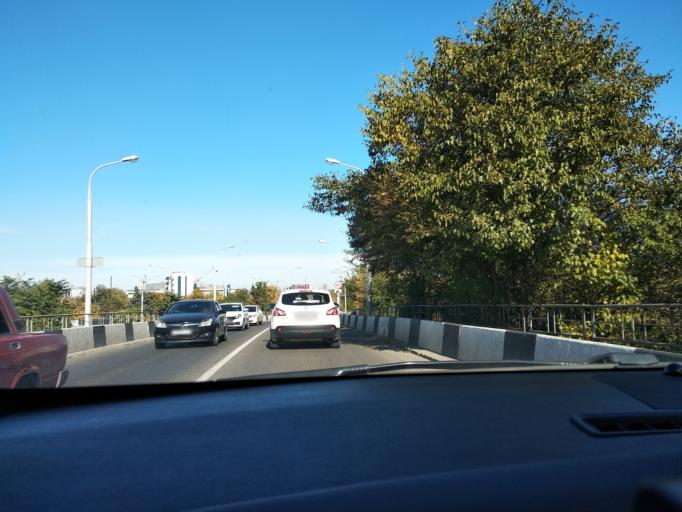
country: RU
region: Adygeya
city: Yablonovskiy
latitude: 44.9968
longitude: 38.9588
